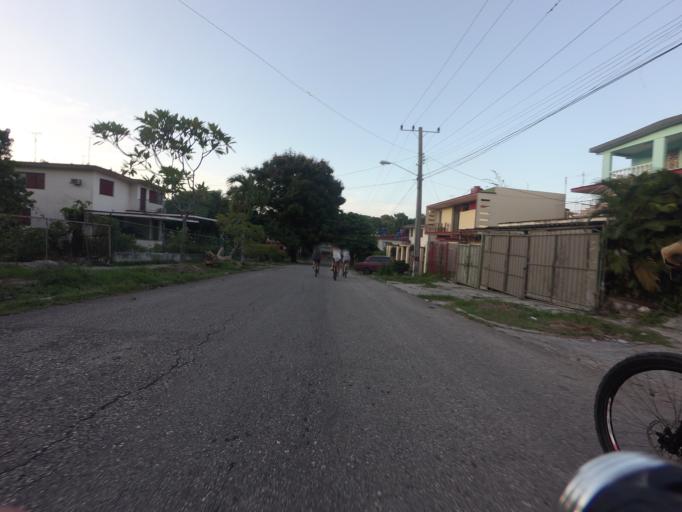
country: CU
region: La Habana
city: Cerro
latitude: 23.1148
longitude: -82.4057
